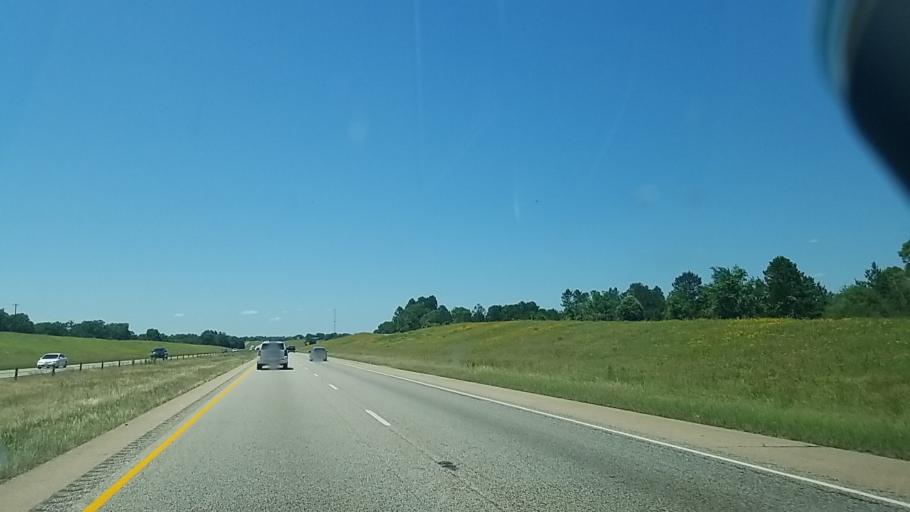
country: US
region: Texas
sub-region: Leon County
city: Buffalo
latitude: 31.4041
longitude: -96.0375
